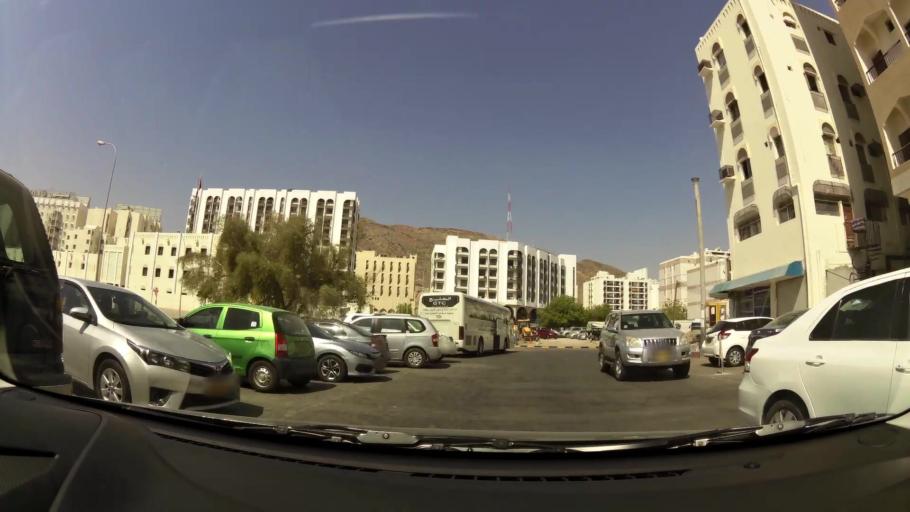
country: OM
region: Muhafazat Masqat
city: Muscat
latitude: 23.5964
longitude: 58.5431
